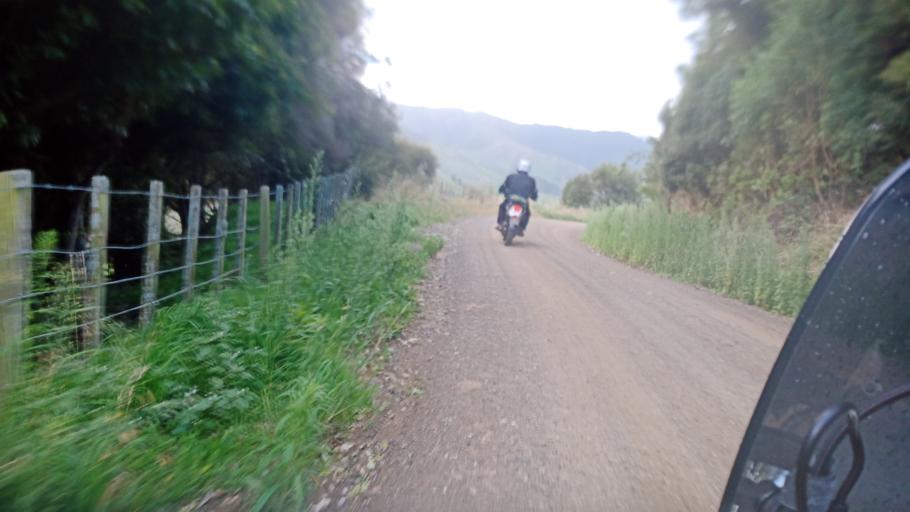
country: NZ
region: Gisborne
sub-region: Gisborne District
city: Gisborne
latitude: -38.4689
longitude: 177.6198
